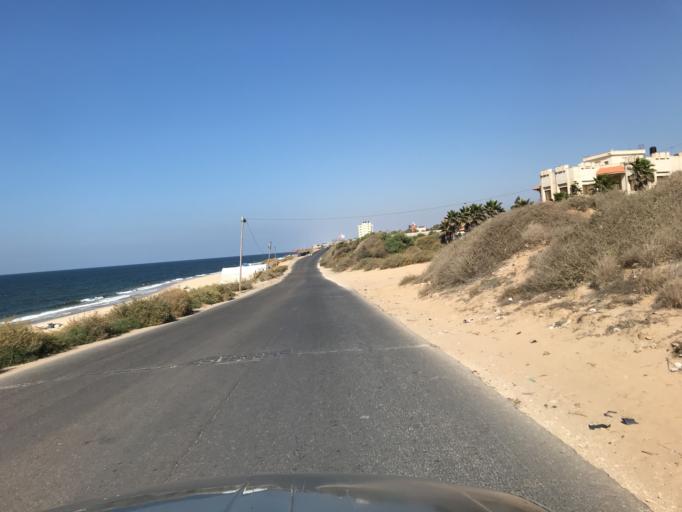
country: PS
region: Gaza Strip
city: Dayr al Balah
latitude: 31.4421
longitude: 34.3550
